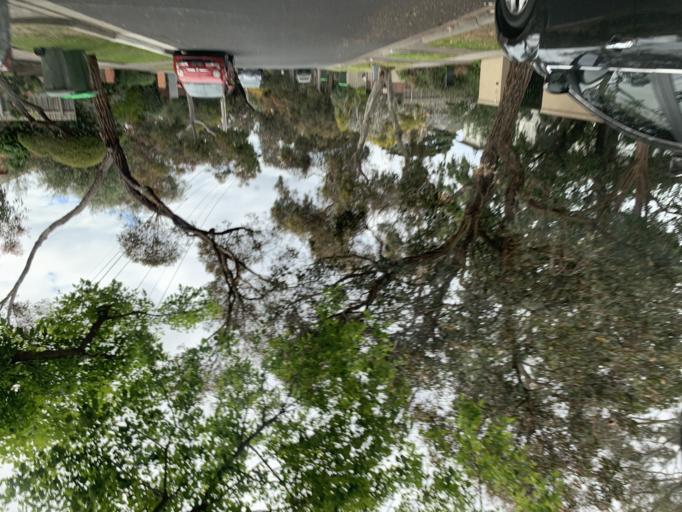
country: AU
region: Victoria
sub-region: Bayside
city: Cheltenham
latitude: -37.9729
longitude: 145.0407
